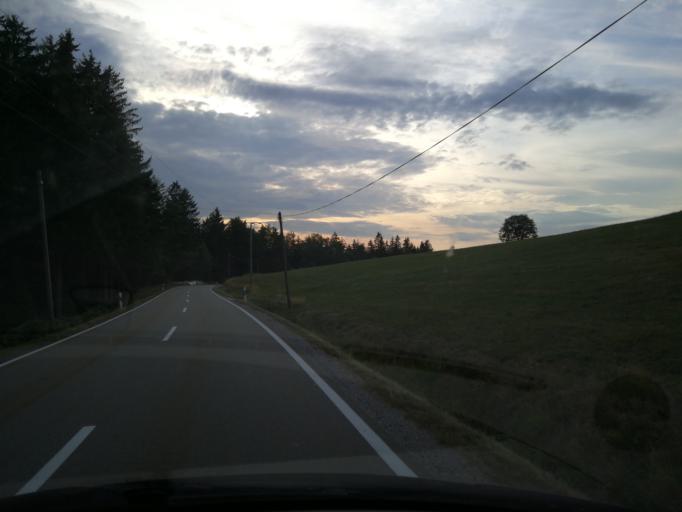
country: DE
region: Bavaria
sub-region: Lower Bavaria
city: Haibach
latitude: 49.0311
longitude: 12.7615
